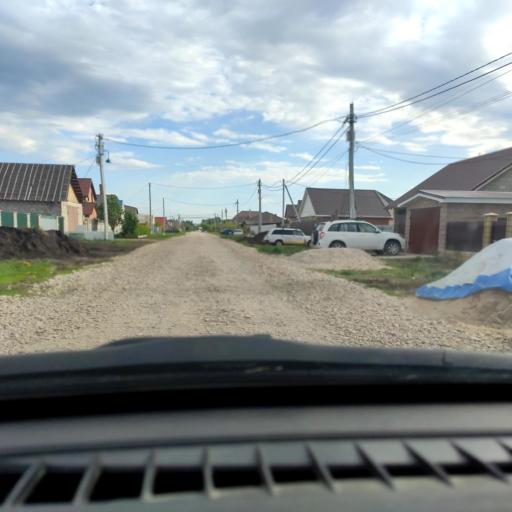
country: RU
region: Samara
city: Tol'yatti
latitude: 53.5649
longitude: 49.4076
